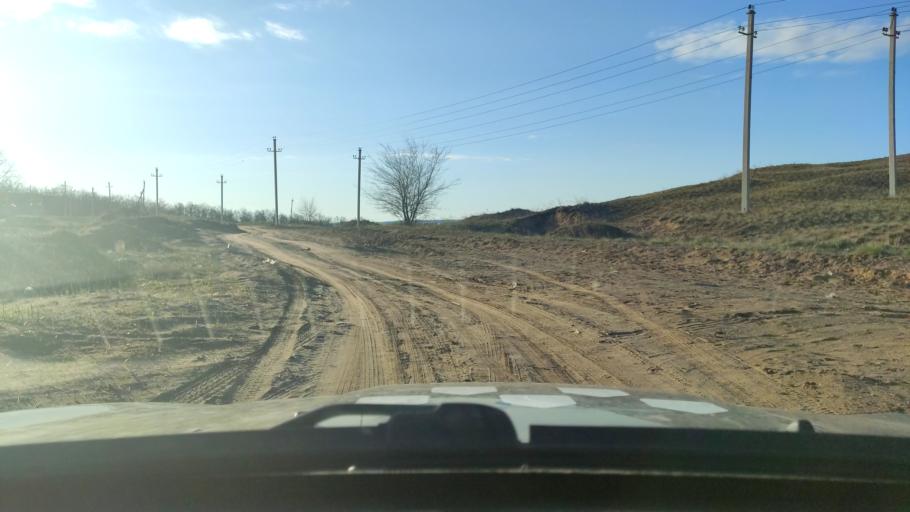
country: RU
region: Samara
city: Zhigulevsk
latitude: 53.4796
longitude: 49.5316
